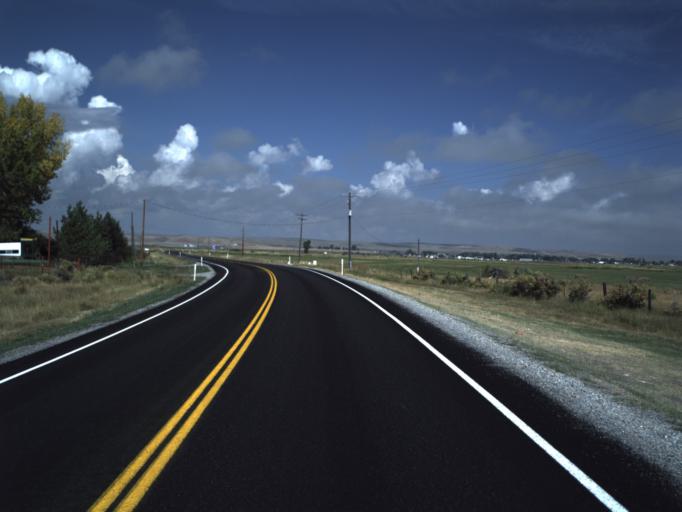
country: US
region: Utah
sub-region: Rich County
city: Randolph
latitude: 41.6364
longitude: -111.1793
